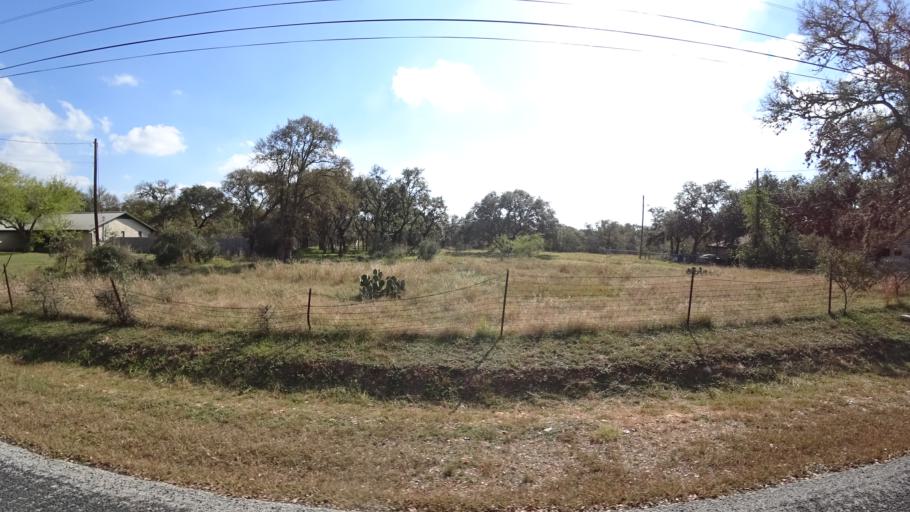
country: US
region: Texas
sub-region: Travis County
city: Shady Hollow
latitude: 30.1788
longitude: -97.8484
